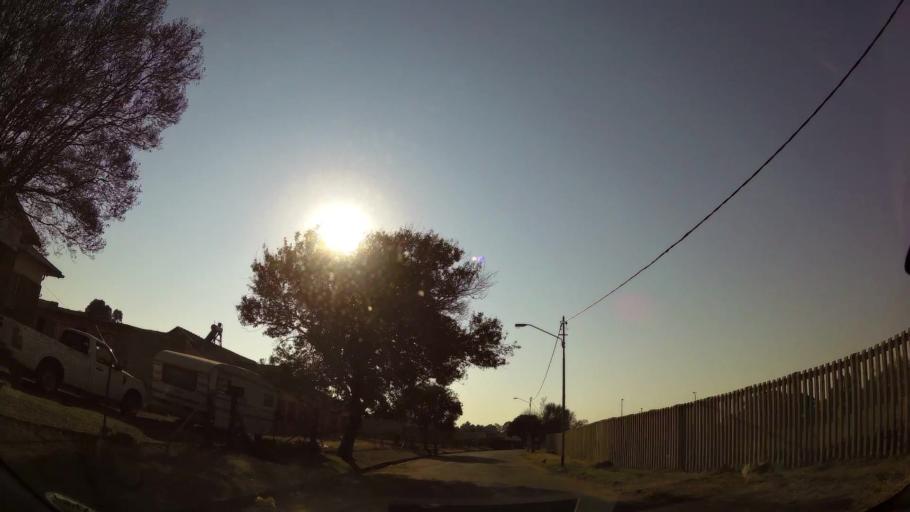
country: ZA
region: Gauteng
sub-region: City of Johannesburg Metropolitan Municipality
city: Modderfontein
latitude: -26.1575
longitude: 28.2013
